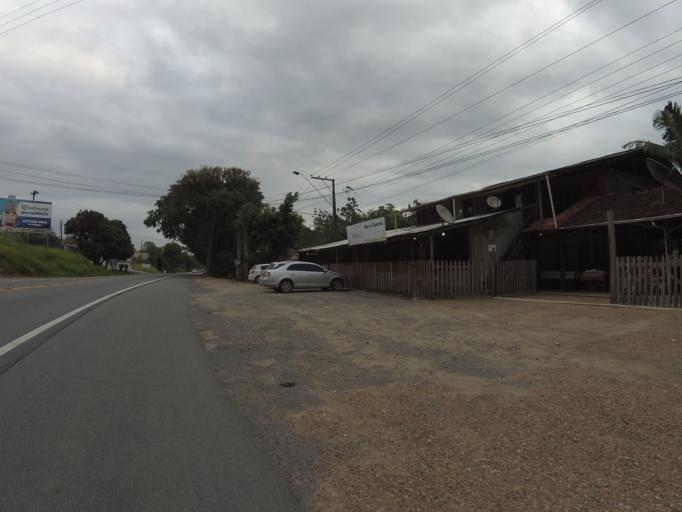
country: BR
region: Santa Catarina
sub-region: Blumenau
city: Blumenau
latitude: -26.8678
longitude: -49.1426
